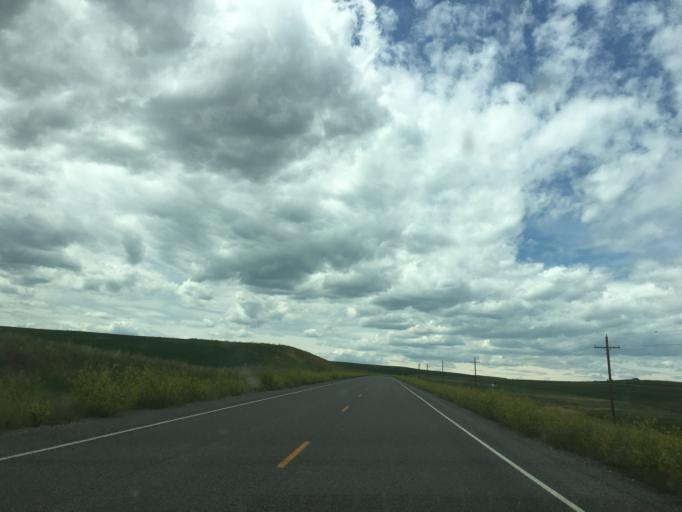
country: US
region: Montana
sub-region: Teton County
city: Choteau
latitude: 48.1372
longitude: -112.3952
